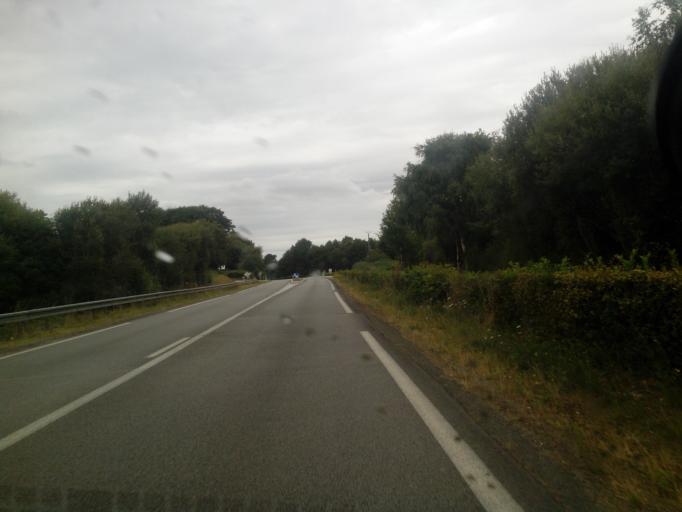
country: FR
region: Brittany
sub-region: Departement du Morbihan
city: Kervignac
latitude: 47.7582
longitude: -3.2465
